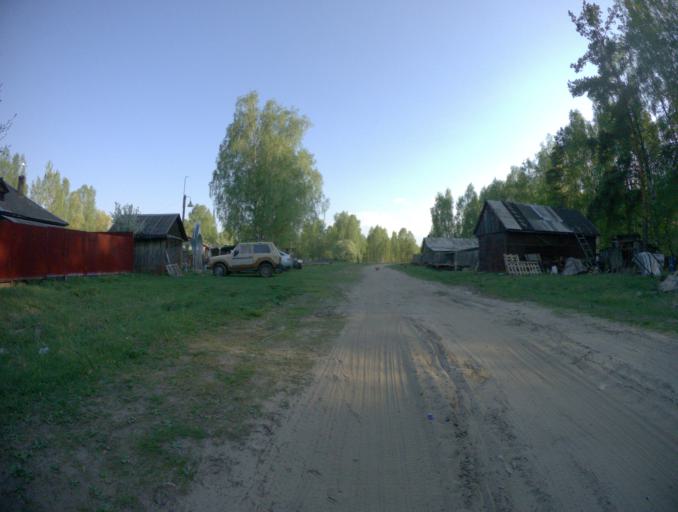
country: RU
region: Vladimir
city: Vyazniki
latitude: 56.3604
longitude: 42.1385
